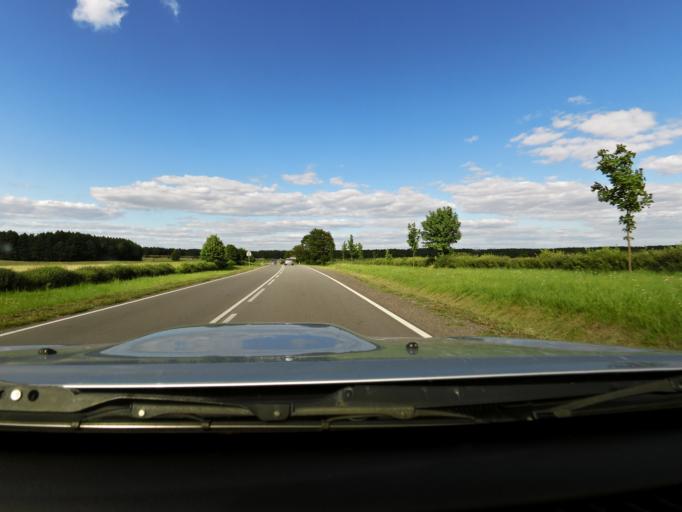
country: PL
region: Warmian-Masurian Voivodeship
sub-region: Powiat elcki
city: Elk
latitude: 53.8199
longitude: 22.2796
